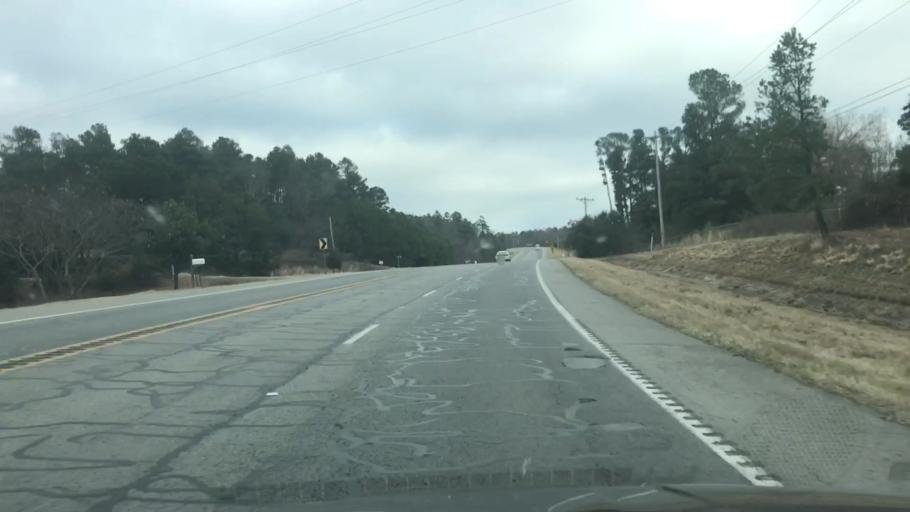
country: US
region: Arkansas
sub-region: Scott County
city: Waldron
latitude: 34.8135
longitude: -94.0400
